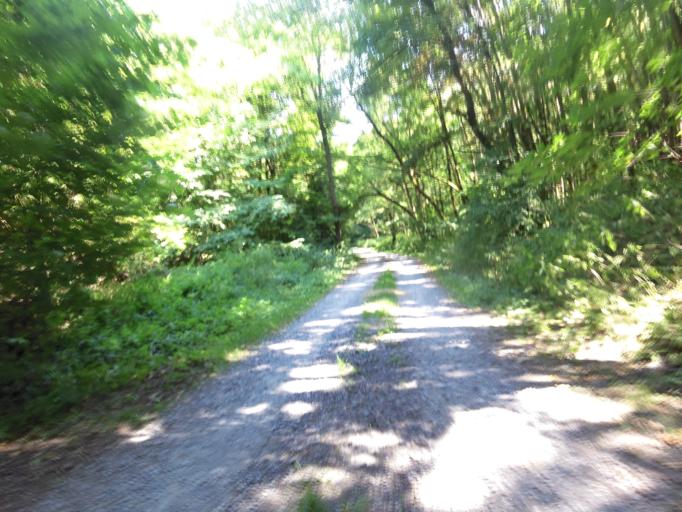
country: DE
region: Bavaria
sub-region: Regierungsbezirk Unterfranken
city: Rimpar
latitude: 49.8303
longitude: 9.9525
